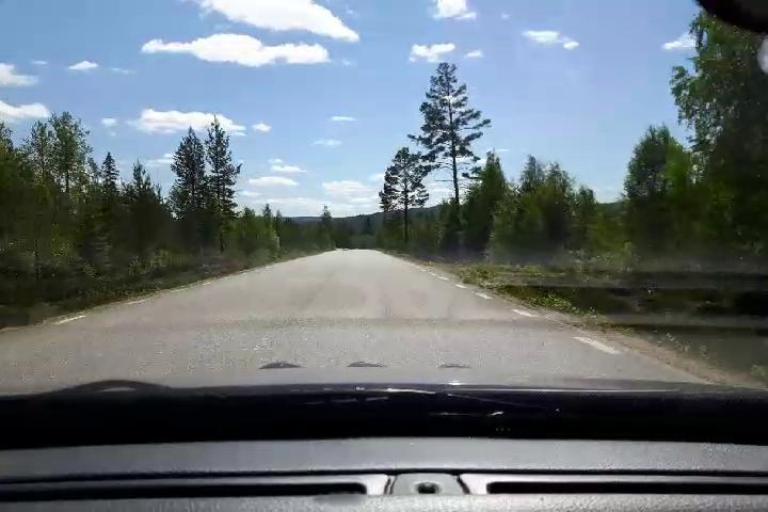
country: SE
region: Gaevleborg
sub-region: Ljusdals Kommun
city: Farila
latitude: 62.0041
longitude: 15.2401
